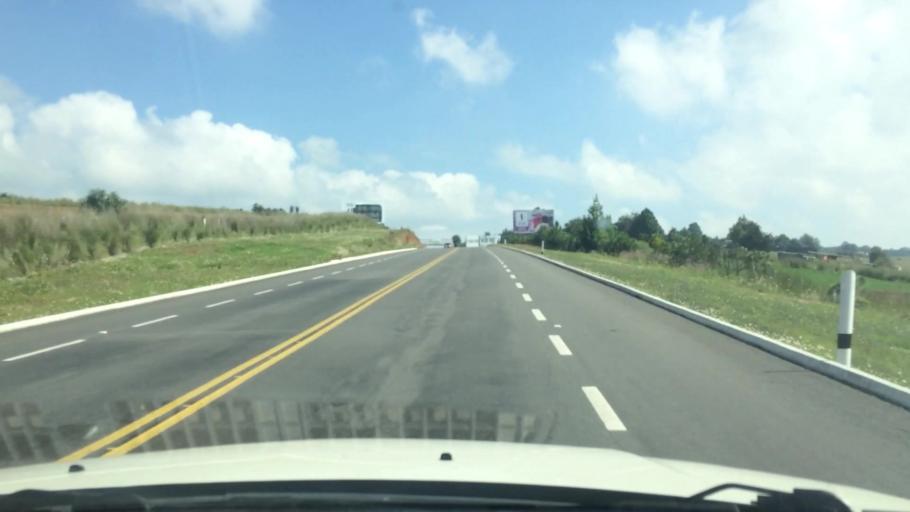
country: MX
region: Mexico
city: Amanalco de Becerra
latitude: 19.3253
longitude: -99.9995
